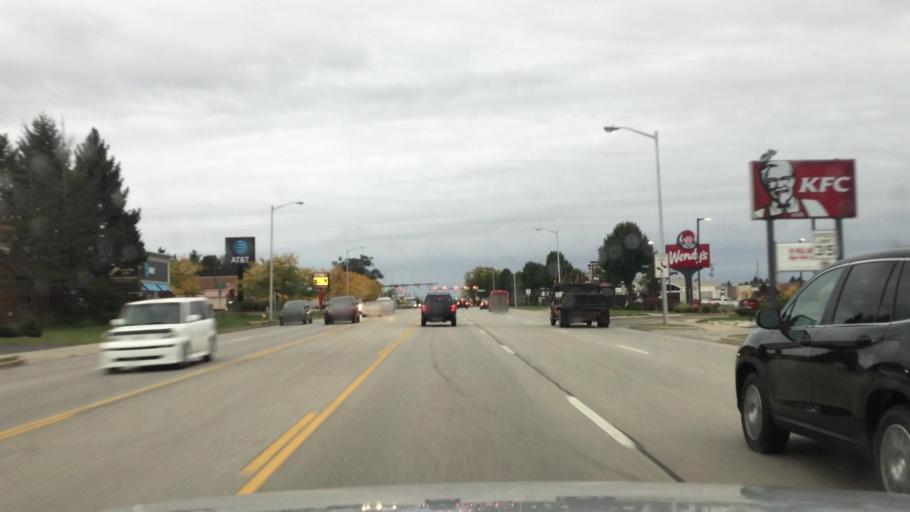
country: US
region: Michigan
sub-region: Kalamazoo County
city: Portage
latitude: 42.2326
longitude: -85.5896
